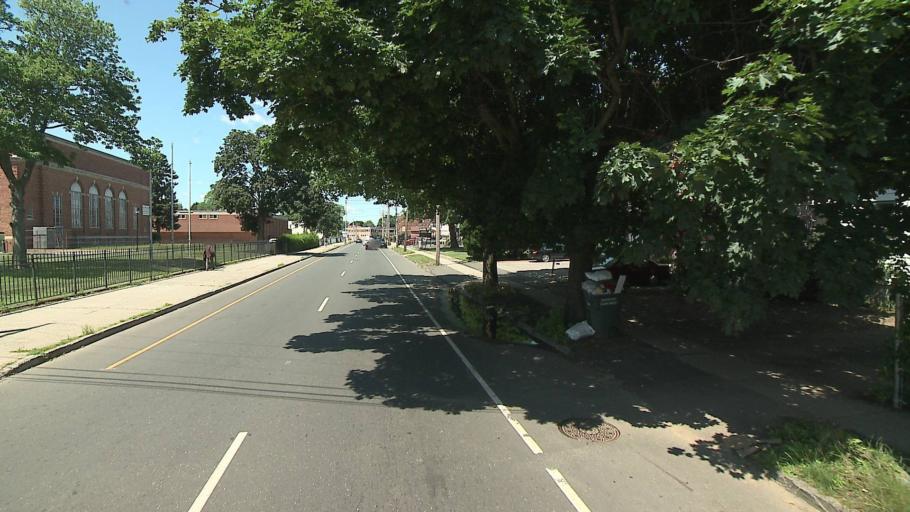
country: US
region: Connecticut
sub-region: Fairfield County
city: Bridgeport
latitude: 41.1741
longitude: -73.2058
